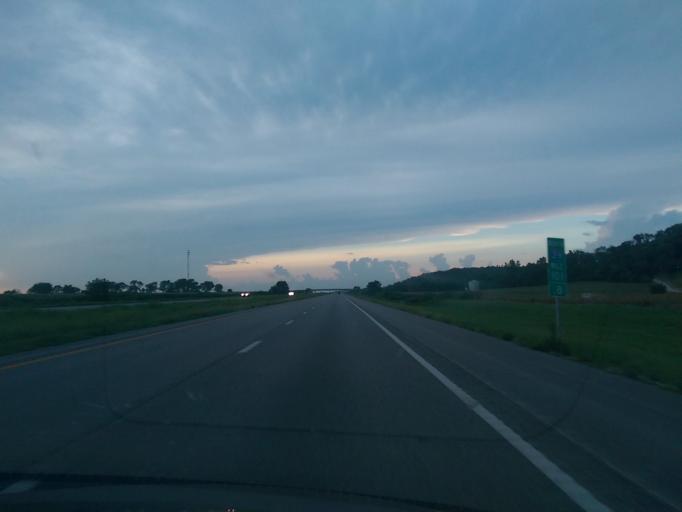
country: US
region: Missouri
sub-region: Atchison County
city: Rock Port
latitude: 40.2925
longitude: -95.4837
